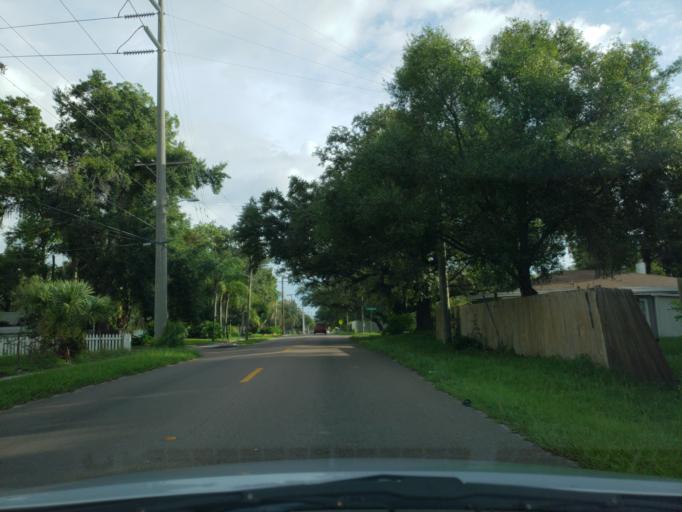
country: US
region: Florida
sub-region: Hillsborough County
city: Temple Terrace
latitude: 28.0012
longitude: -82.4347
